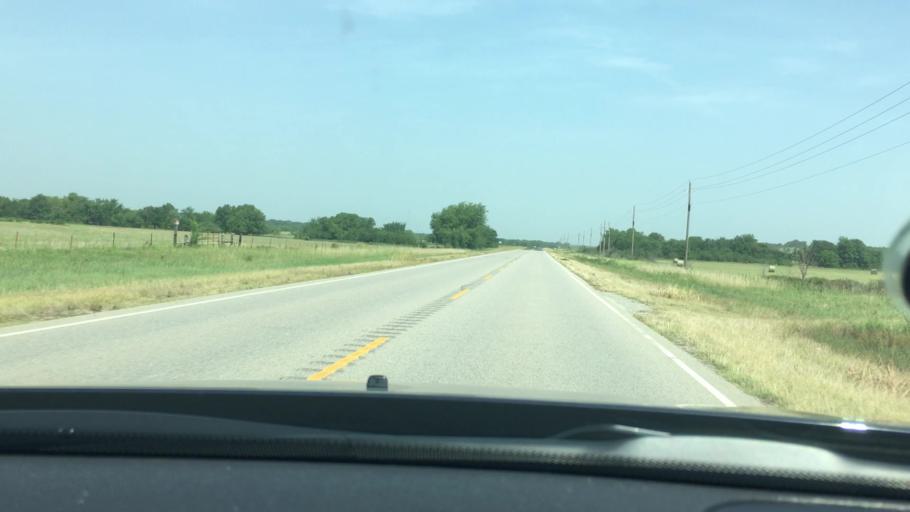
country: US
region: Oklahoma
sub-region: Atoka County
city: Atoka
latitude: 34.4287
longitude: -96.1958
